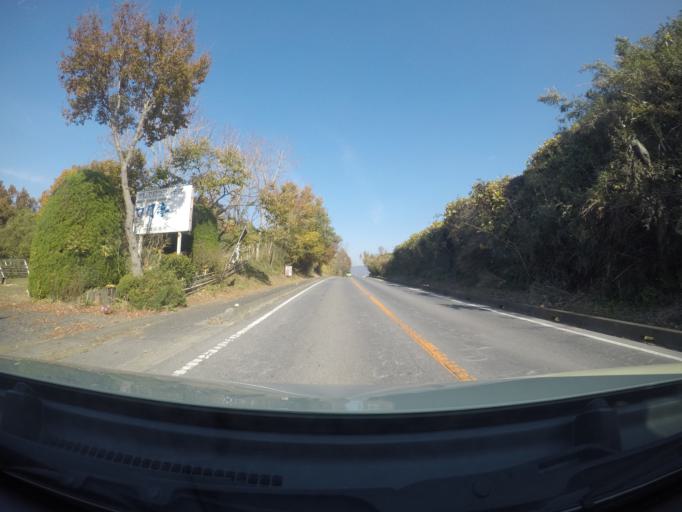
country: JP
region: Ibaraki
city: Makabe
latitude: 36.2644
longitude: 140.0925
